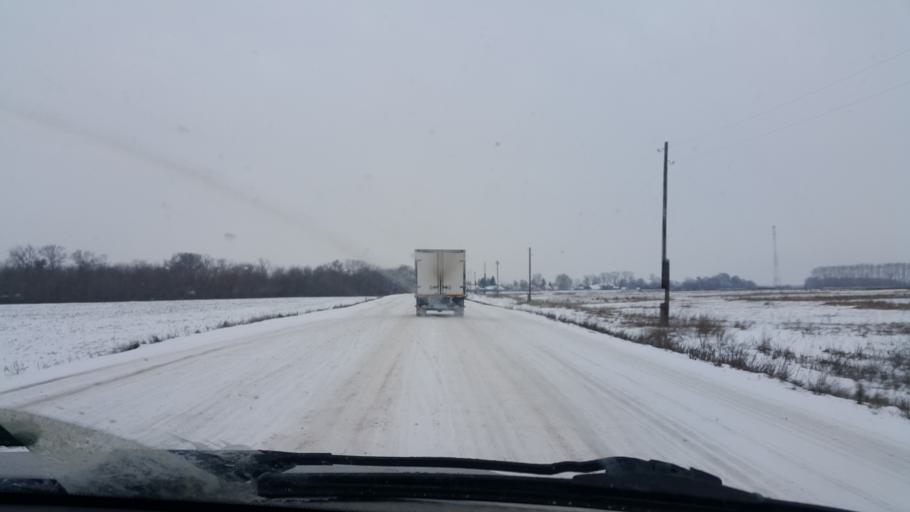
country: RU
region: Tambov
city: Inzhavino
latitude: 52.4710
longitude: 42.3948
